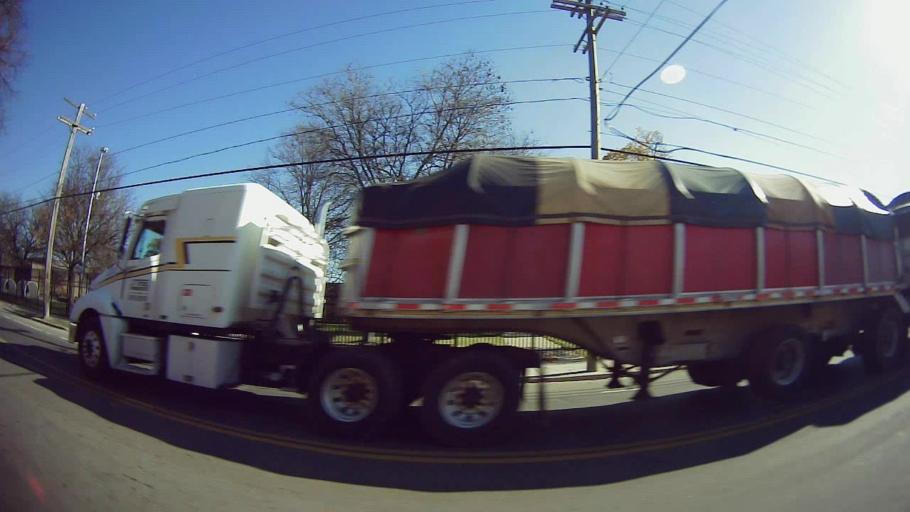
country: US
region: Michigan
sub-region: Wayne County
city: Dearborn
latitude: 42.3666
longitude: -83.1583
